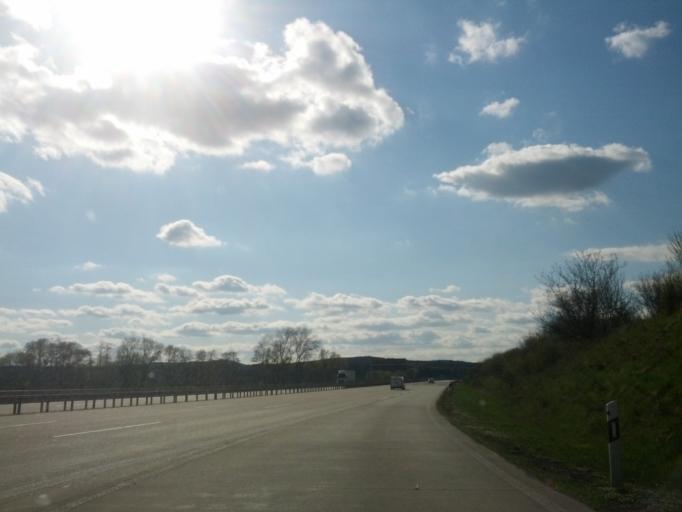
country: DE
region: Thuringia
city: Waltershausen
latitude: 50.9202
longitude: 10.5444
